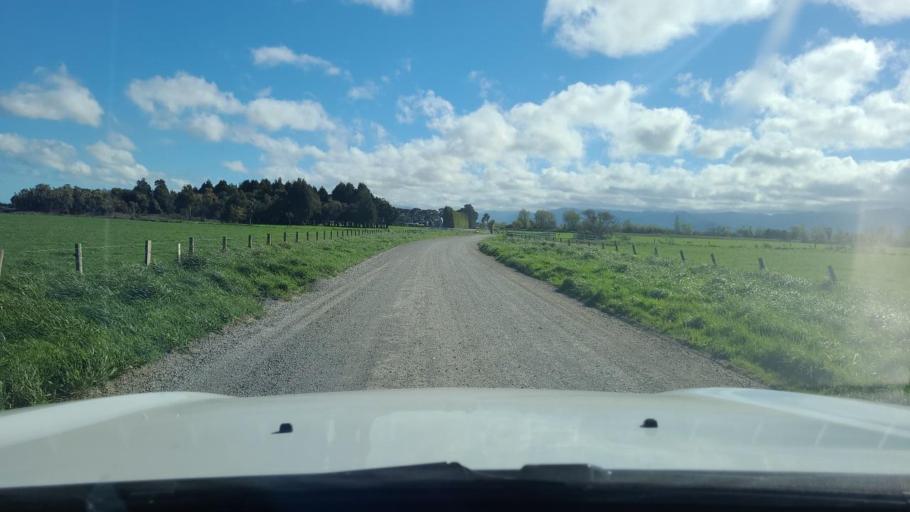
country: NZ
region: Wellington
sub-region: South Wairarapa District
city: Waipawa
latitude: -41.1605
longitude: 175.3633
